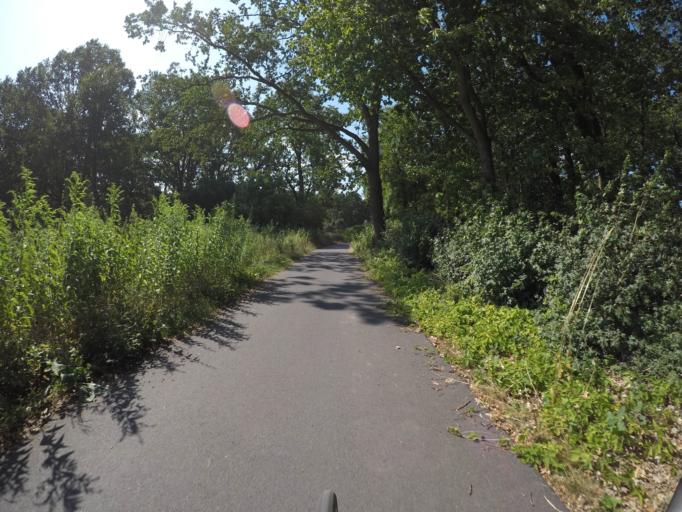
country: DE
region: Berlin
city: Kladow
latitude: 52.4898
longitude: 13.1437
